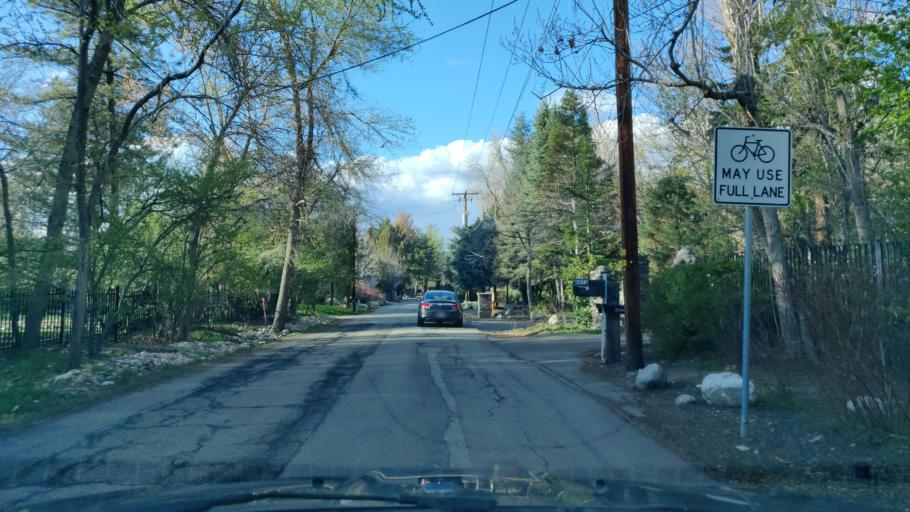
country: US
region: Utah
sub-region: Salt Lake County
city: Cottonwood Heights
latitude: 40.6410
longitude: -111.8248
